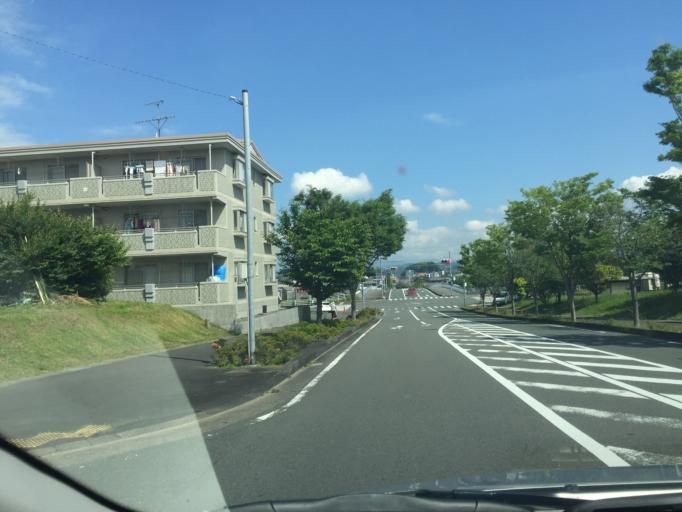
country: JP
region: Shizuoka
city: Kakegawa
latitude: 34.7679
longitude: 137.9957
